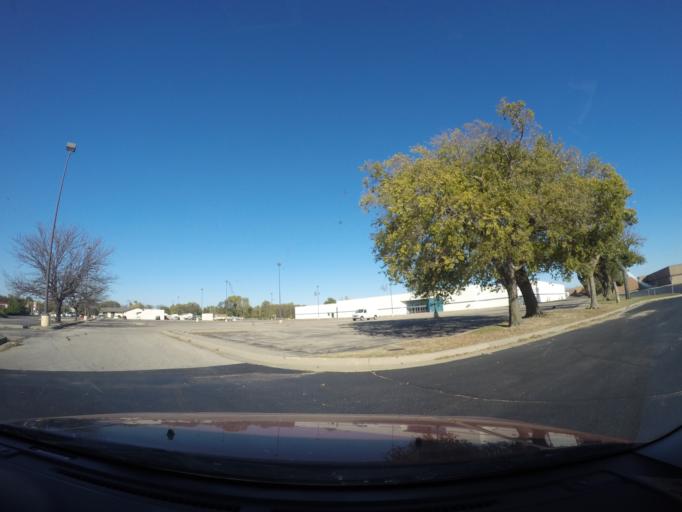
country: US
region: Kansas
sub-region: Sedgwick County
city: Wichita
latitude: 37.6783
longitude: -97.3936
